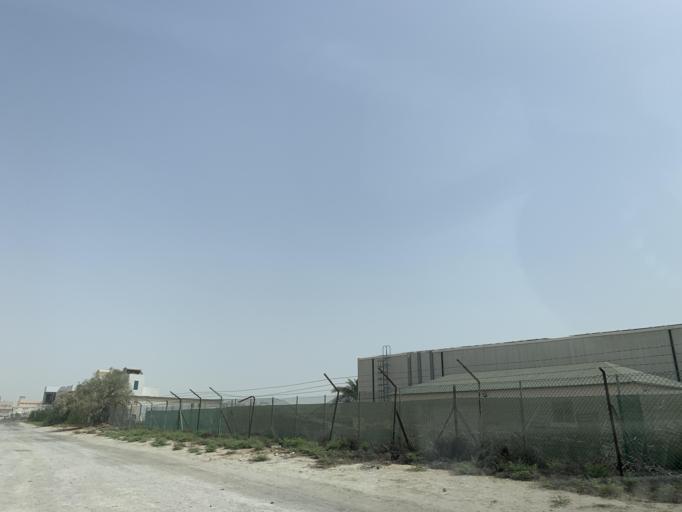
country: BH
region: Northern
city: Madinat `Isa
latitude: 26.1716
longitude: 50.5264
